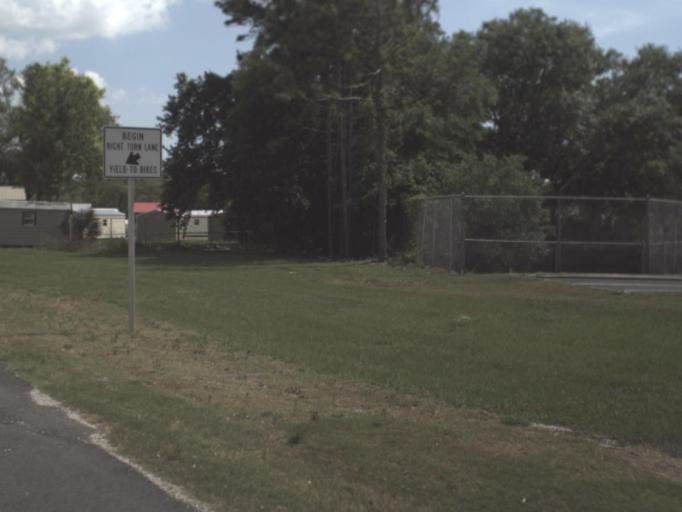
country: US
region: Florida
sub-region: Saint Johns County
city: Fruit Cove
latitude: 30.2031
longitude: -81.5749
